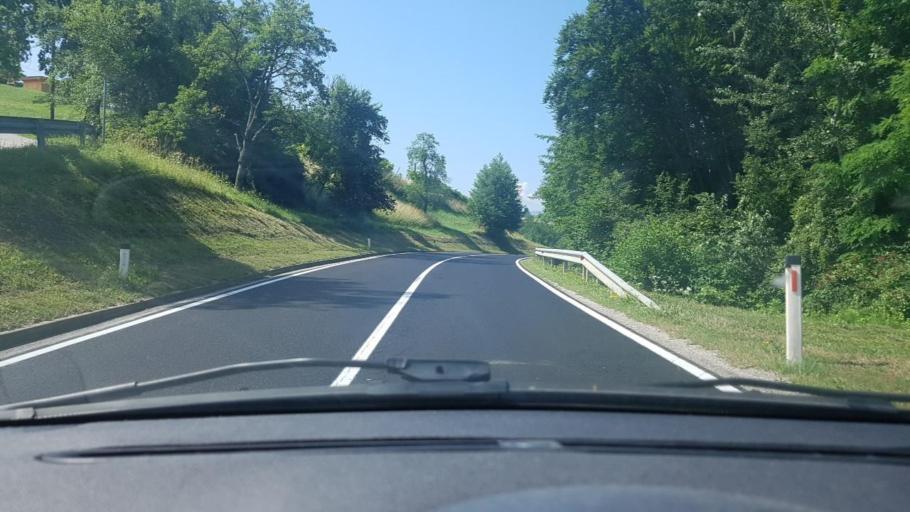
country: SI
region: Sentilj
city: Sentilj v Slov. Goricah
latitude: 46.6873
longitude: 15.6670
